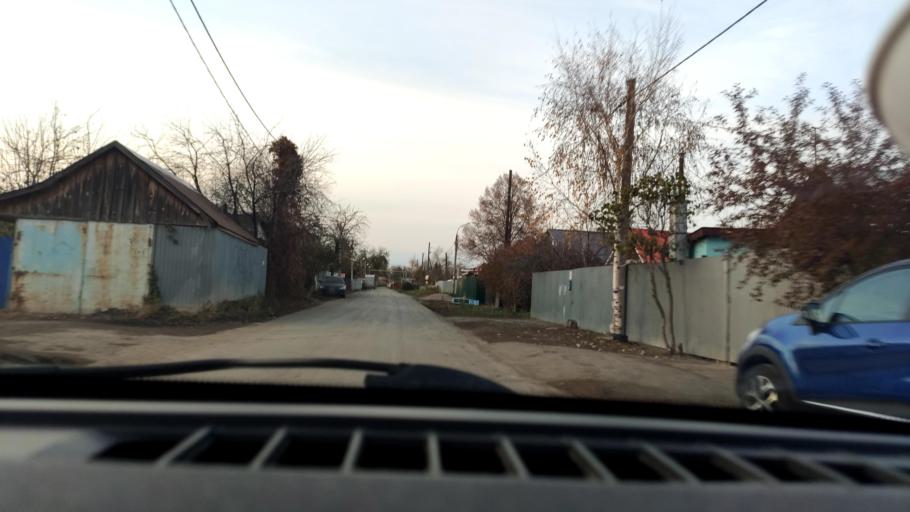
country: RU
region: Samara
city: Samara
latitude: 53.1380
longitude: 50.1367
